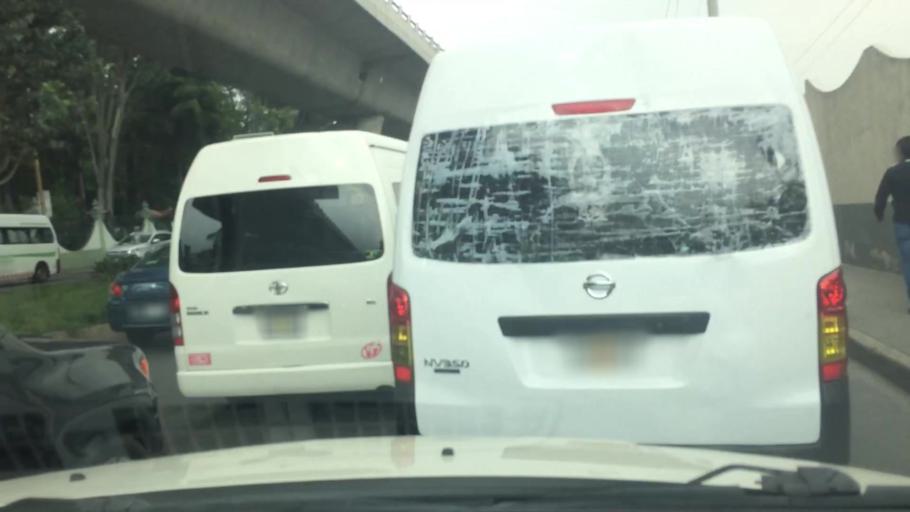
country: MX
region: Mexico City
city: Miguel Hidalgo
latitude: 19.4432
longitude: -99.2220
